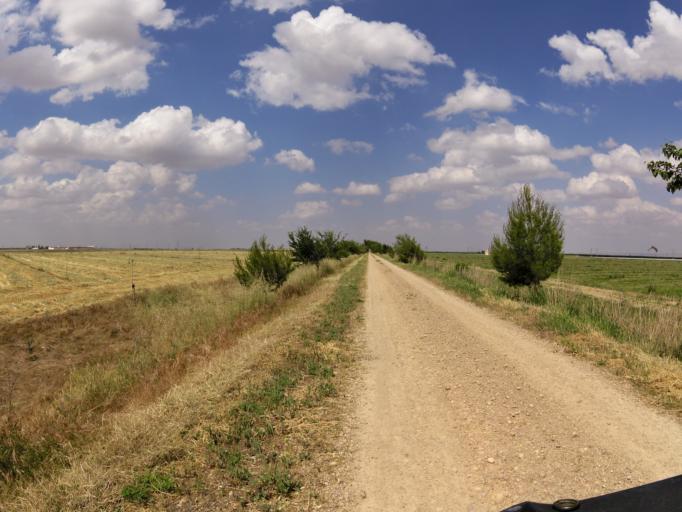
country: ES
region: Castille-La Mancha
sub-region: Provincia de Albacete
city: Pozuelo
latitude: 38.9234
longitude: -2.0028
